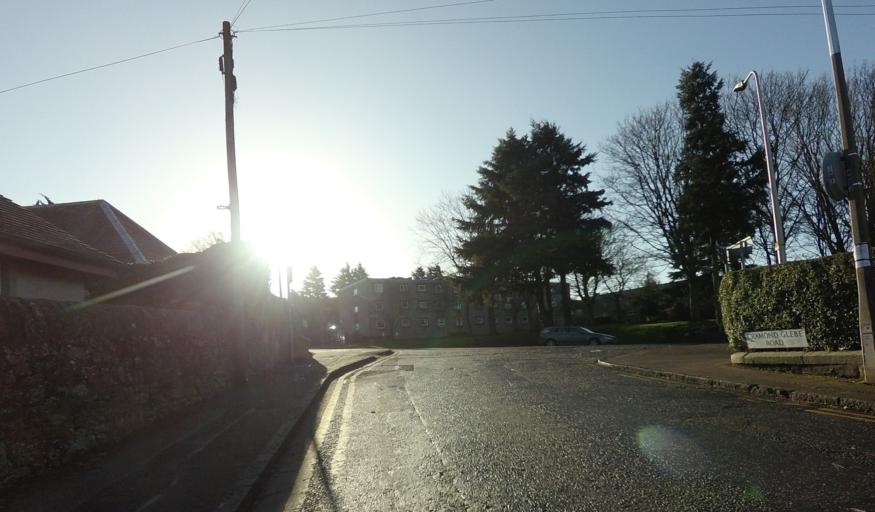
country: GB
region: Scotland
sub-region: Fife
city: Aberdour
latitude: 55.9756
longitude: -3.2993
